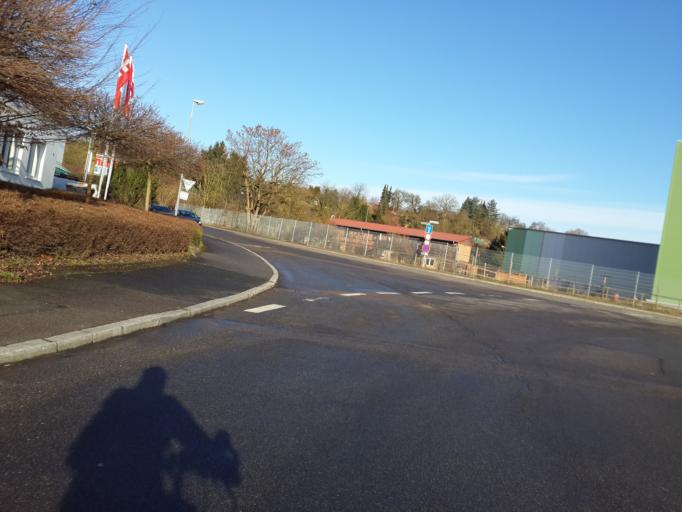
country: DE
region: Baden-Wuerttemberg
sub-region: Regierungsbezirk Stuttgart
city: Neckarsulm
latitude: 49.1777
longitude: 9.1978
